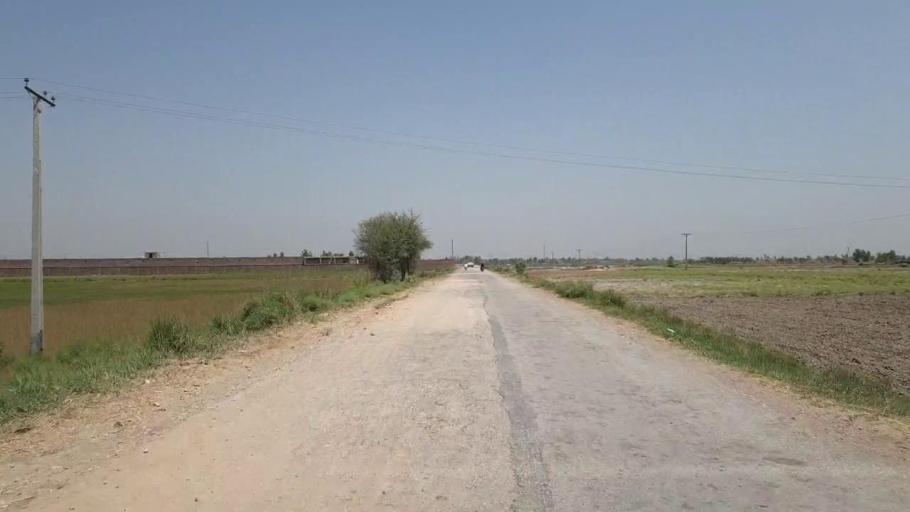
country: PK
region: Sindh
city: Adilpur
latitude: 27.8782
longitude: 69.2863
